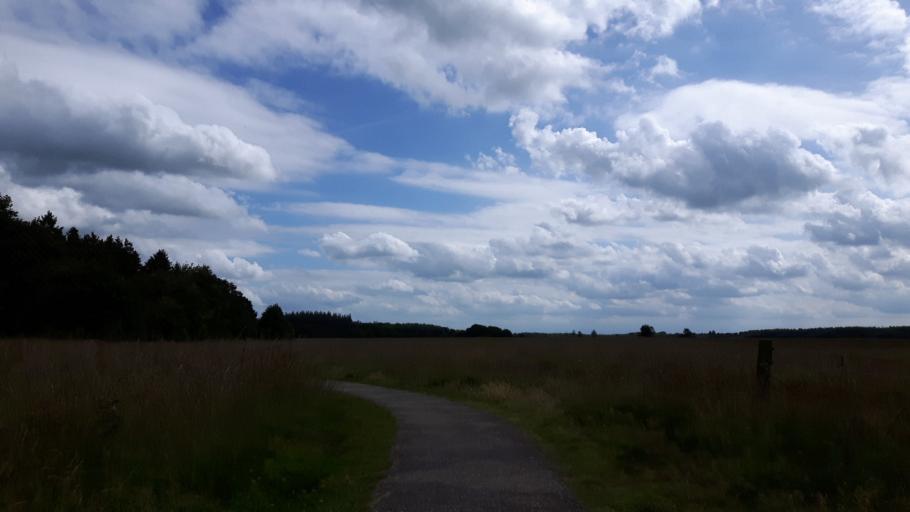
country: NL
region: Friesland
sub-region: Gemeente Smallingerland
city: Drachtstercompagnie
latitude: 53.0616
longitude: 6.2352
